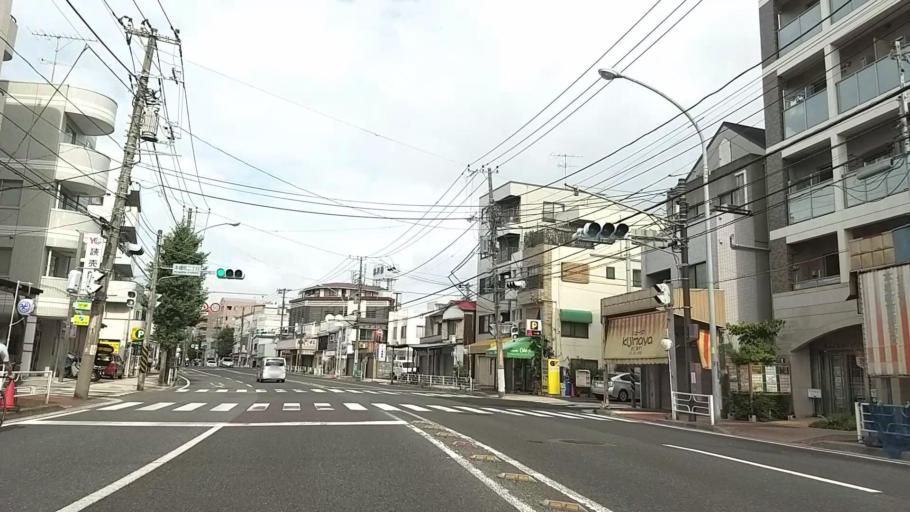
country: JP
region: Kanagawa
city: Yokohama
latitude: 35.4324
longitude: 139.6554
